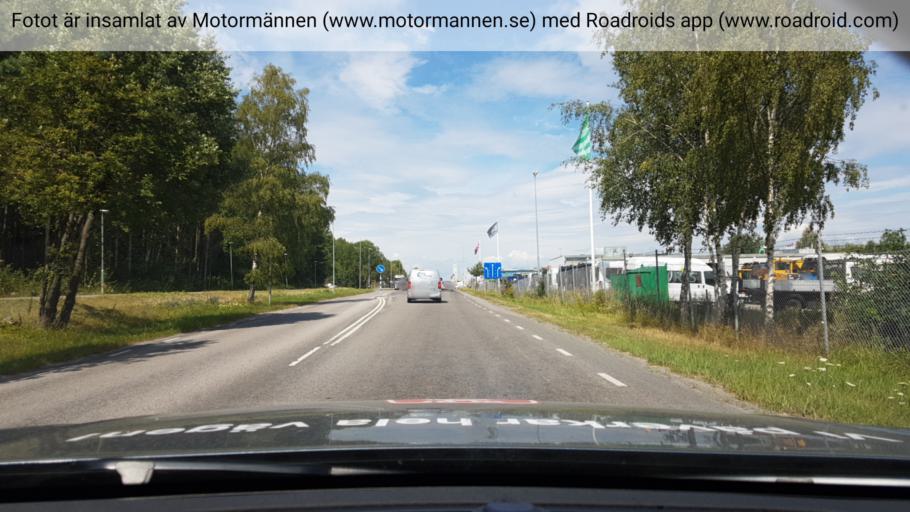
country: SE
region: Stockholm
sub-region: Jarfalla Kommun
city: Jakobsberg
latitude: 59.4047
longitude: 17.8417
